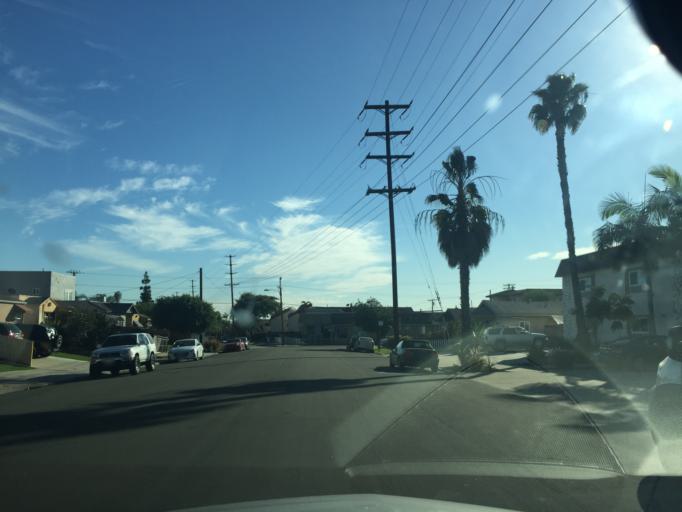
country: US
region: California
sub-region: San Diego County
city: San Diego
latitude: 32.7524
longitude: -117.1218
